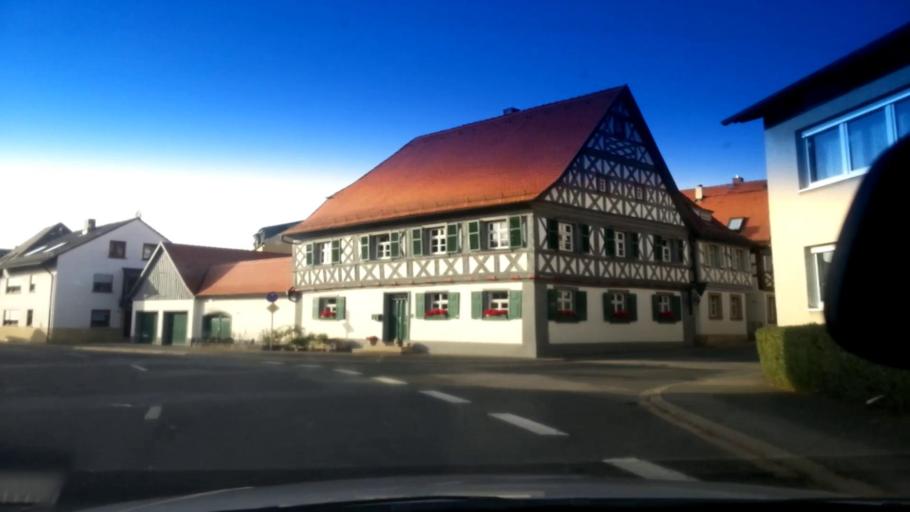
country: DE
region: Bavaria
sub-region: Upper Franconia
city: Schesslitz
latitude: 49.9752
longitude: 11.0354
